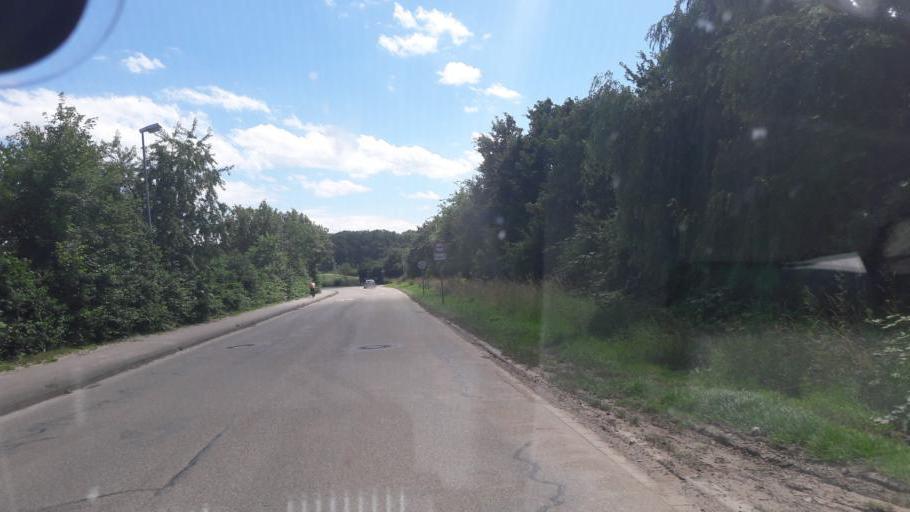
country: DE
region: Baden-Wuerttemberg
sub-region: Karlsruhe Region
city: Karlsdorf-Neuthard
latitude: 49.1224
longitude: 8.5615
